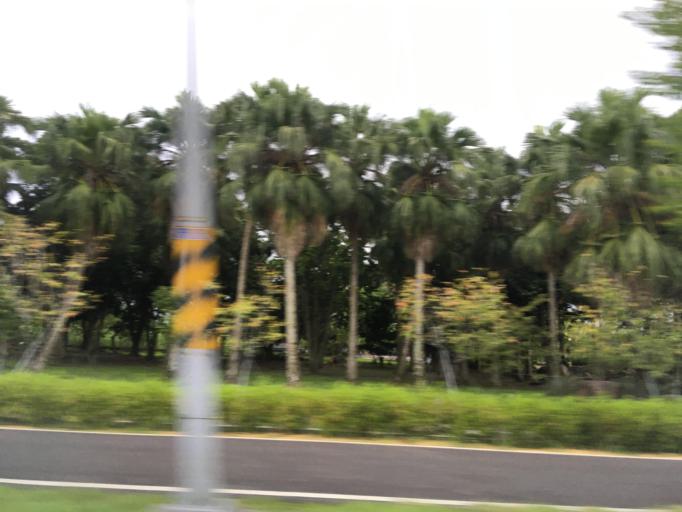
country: TW
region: Taiwan
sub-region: Yilan
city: Yilan
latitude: 24.6772
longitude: 121.6423
